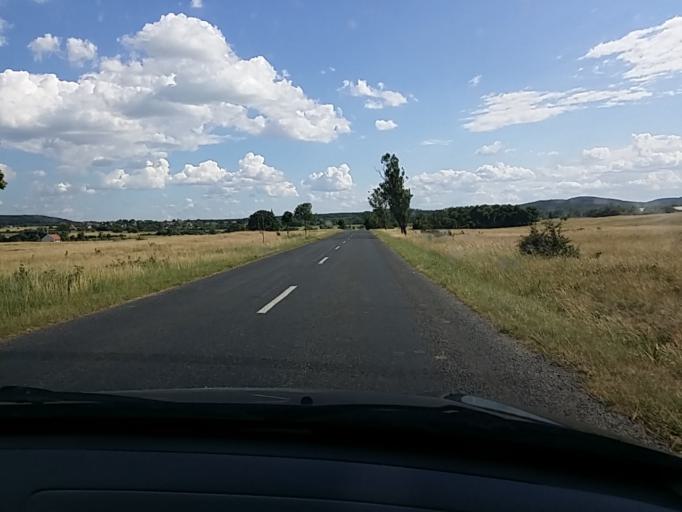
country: HU
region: Veszprem
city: Revfueloep
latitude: 46.8654
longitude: 17.6010
